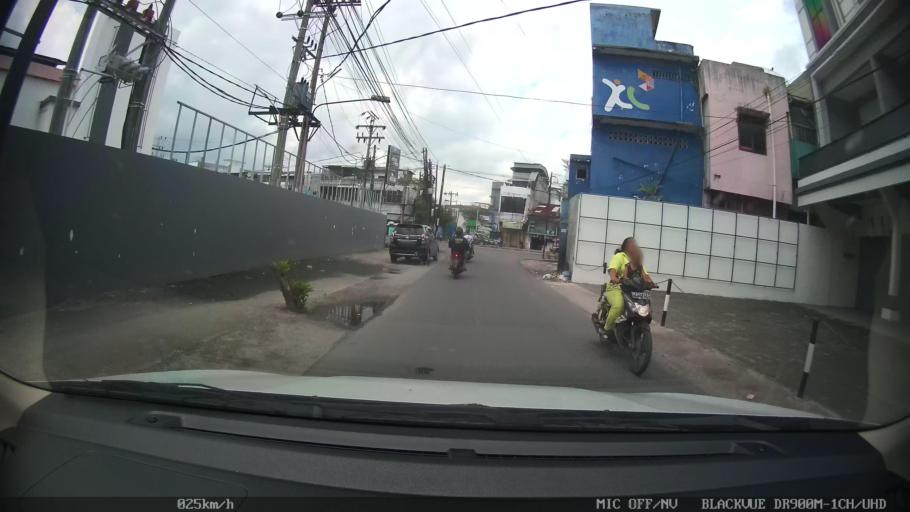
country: ID
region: North Sumatra
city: Medan
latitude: 3.6270
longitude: 98.6680
